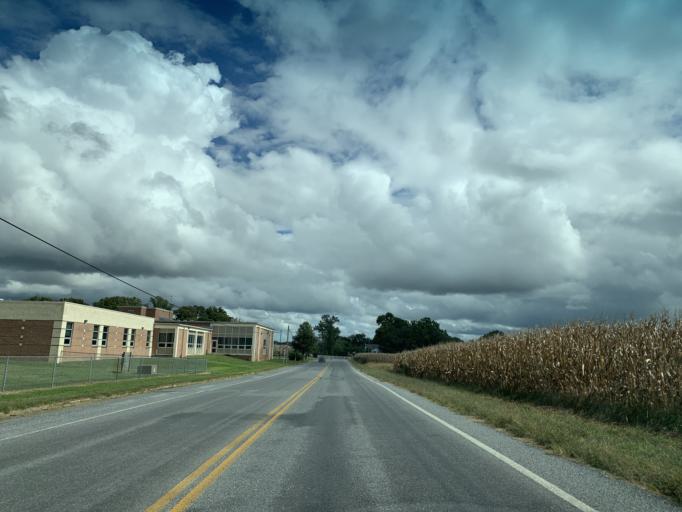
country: US
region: Maryland
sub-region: Caroline County
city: Denton
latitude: 38.9076
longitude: -75.8421
